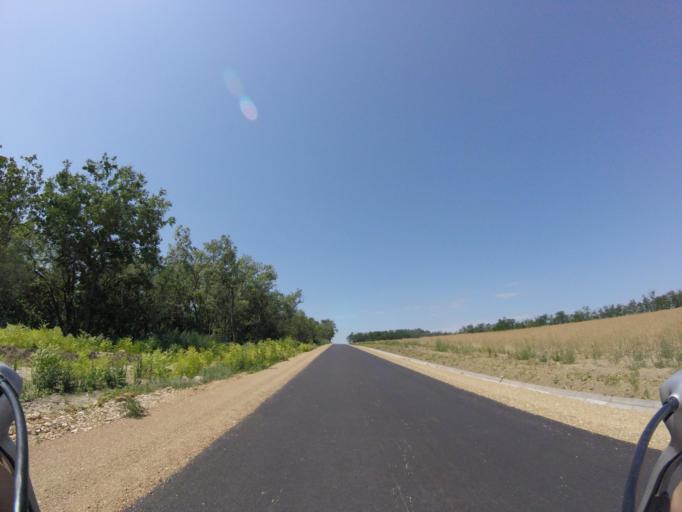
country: HU
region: Fejer
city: Pazmand
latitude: 47.3117
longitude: 18.6947
